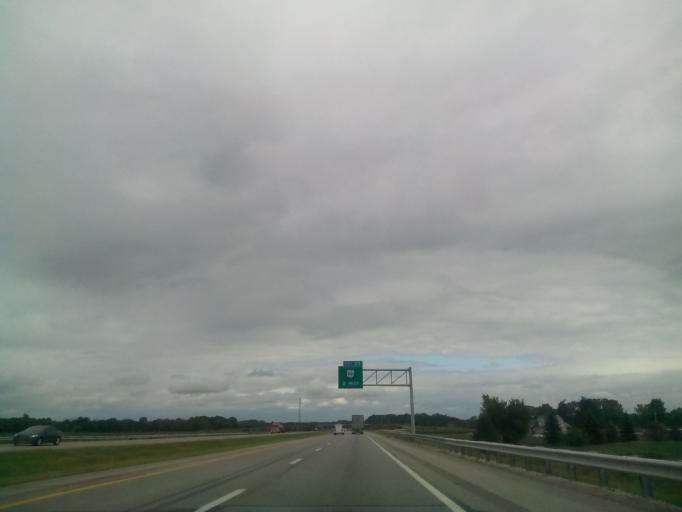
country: US
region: Ohio
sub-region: Fulton County
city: Burlington
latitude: 41.5936
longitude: -84.3599
